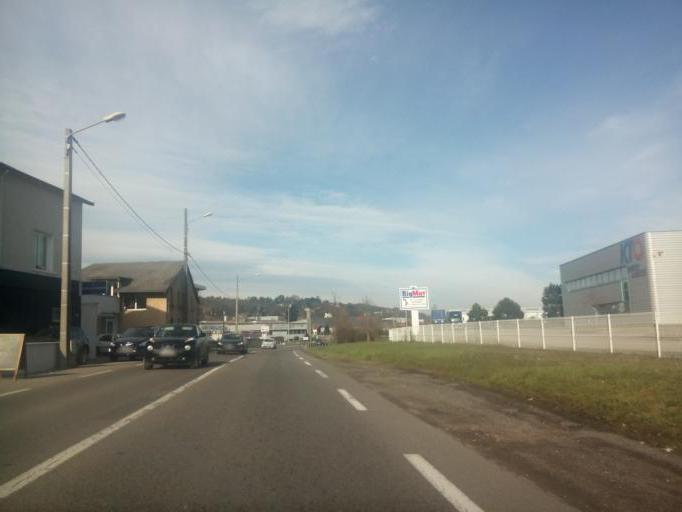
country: FR
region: Rhone-Alpes
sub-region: Departement du Rhone
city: Chaponost
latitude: 45.6958
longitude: 4.7666
